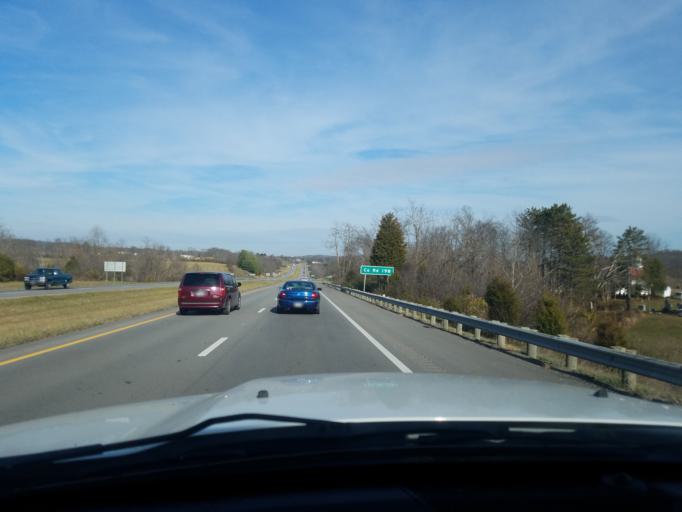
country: US
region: Ohio
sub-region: Athens County
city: Athens
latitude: 39.2613
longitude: -82.1652
